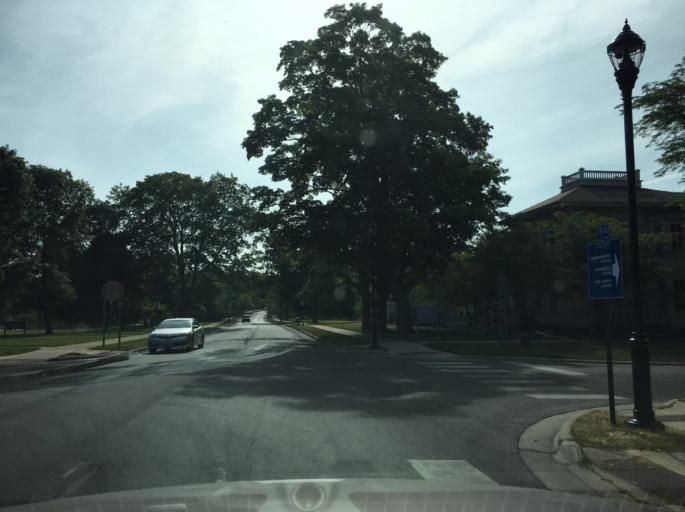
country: US
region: Michigan
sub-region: Grand Traverse County
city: Traverse City
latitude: 44.7559
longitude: -85.6401
